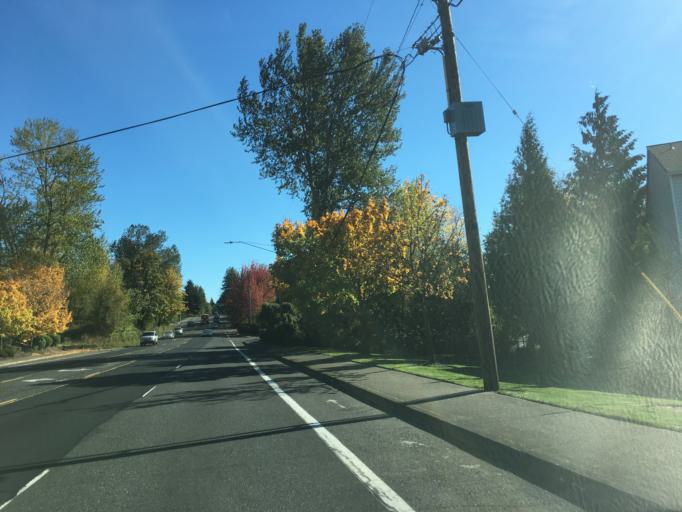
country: US
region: Oregon
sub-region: Multnomah County
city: Gresham
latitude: 45.4845
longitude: -122.3955
